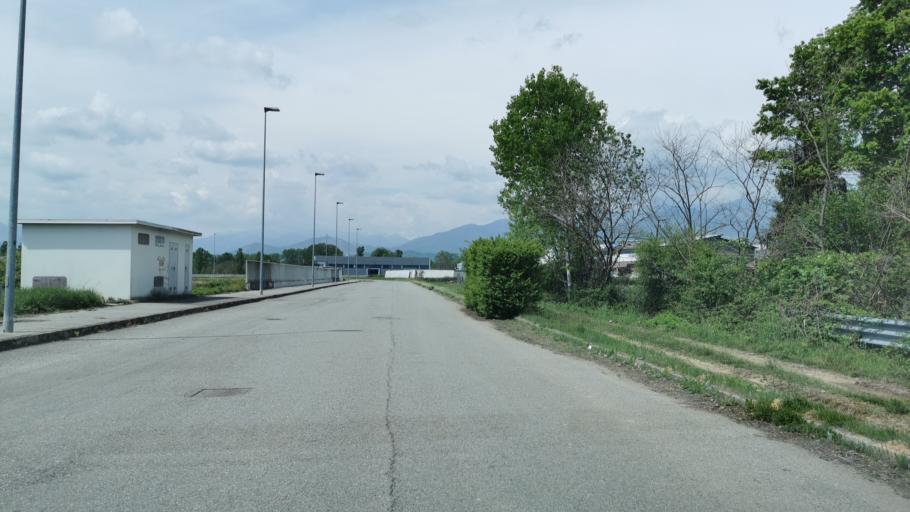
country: IT
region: Piedmont
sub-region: Provincia di Torino
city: Front
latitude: 45.3036
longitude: 7.6688
